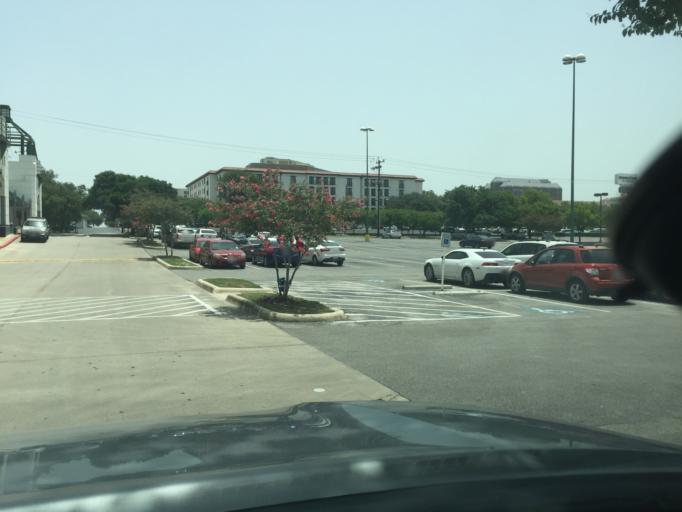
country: US
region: Texas
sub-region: Bexar County
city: Castle Hills
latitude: 29.5221
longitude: -98.4928
